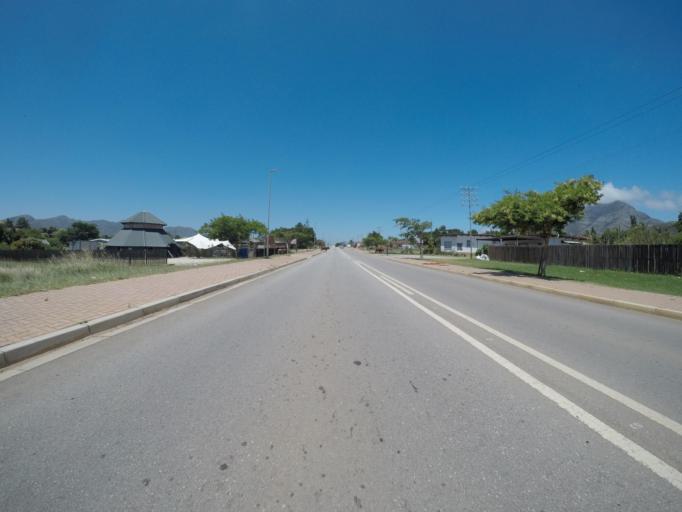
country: ZA
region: Eastern Cape
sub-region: Cacadu District Municipality
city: Kareedouw
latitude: -33.9519
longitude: 24.2917
